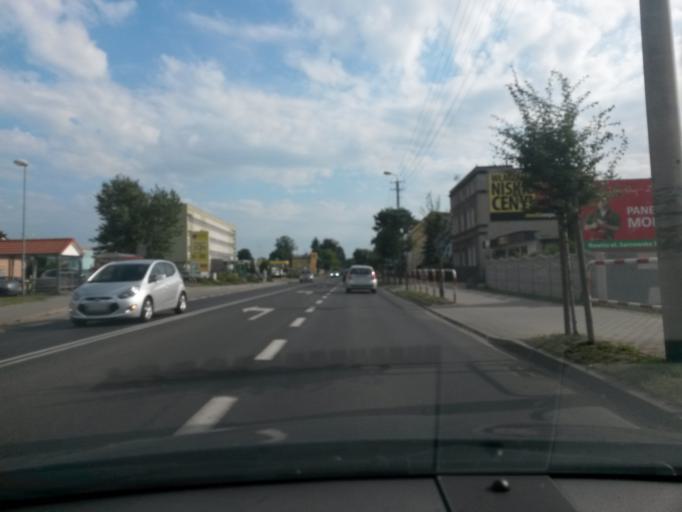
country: PL
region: Greater Poland Voivodeship
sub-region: Powiat rawicki
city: Rawicz
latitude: 51.6136
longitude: 16.8666
